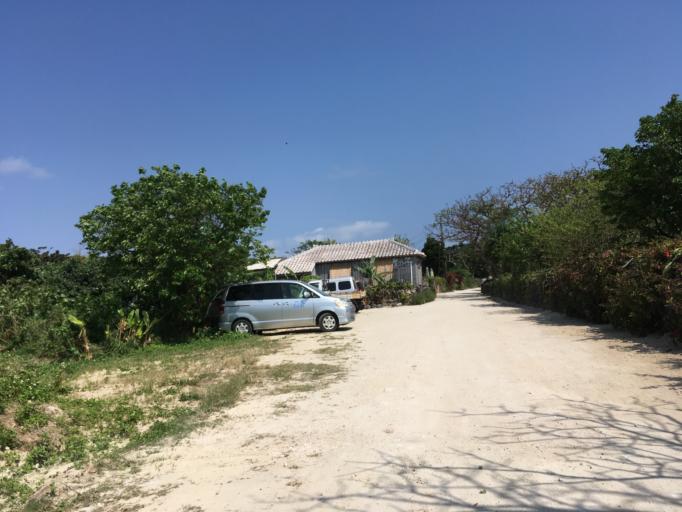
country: JP
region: Okinawa
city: Ishigaki
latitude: 24.3312
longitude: 124.0832
